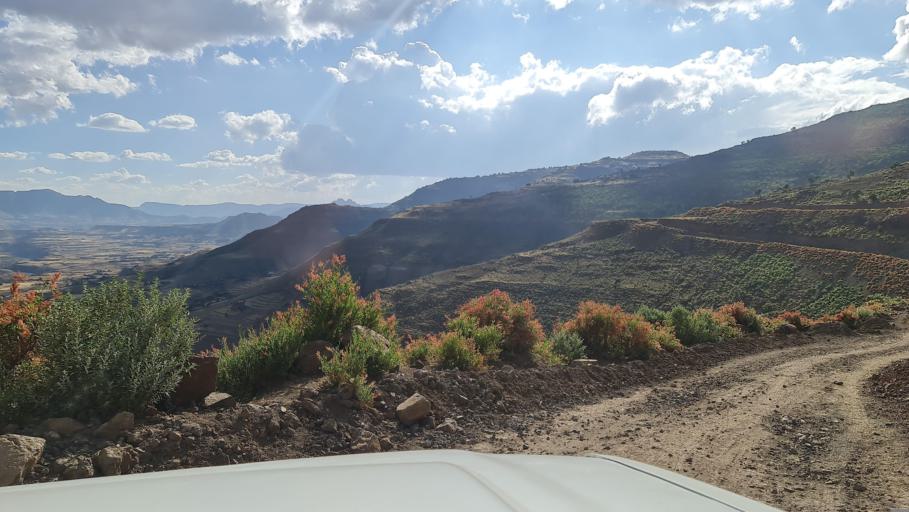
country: ET
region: Amhara
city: Debark'
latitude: 13.1209
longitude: 38.0208
